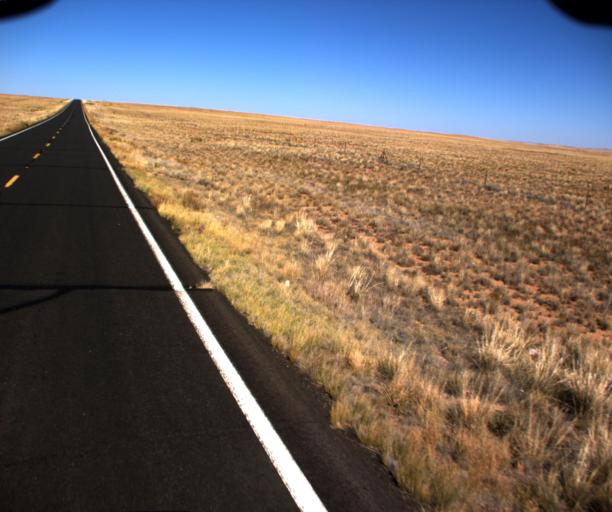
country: US
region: Arizona
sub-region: Navajo County
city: First Mesa
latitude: 35.6239
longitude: -110.4795
